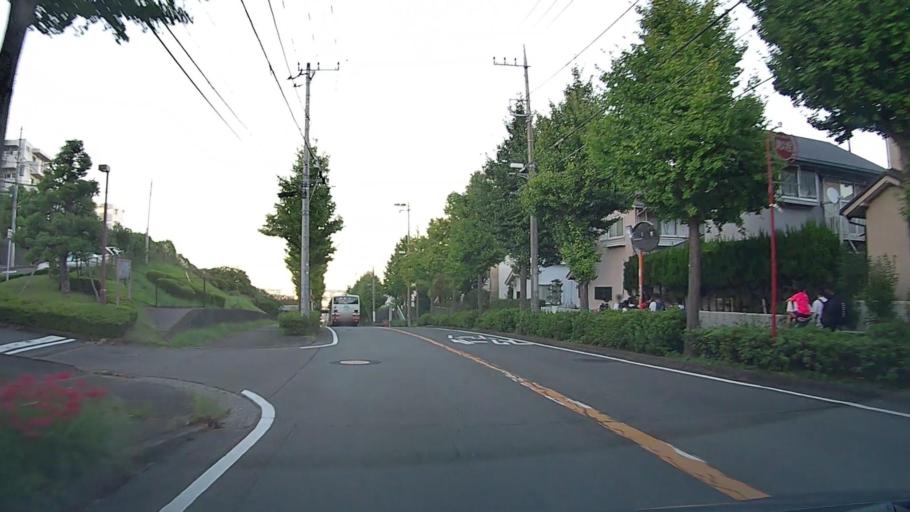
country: JP
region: Tokyo
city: Chofugaoka
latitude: 35.6244
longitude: 139.5268
